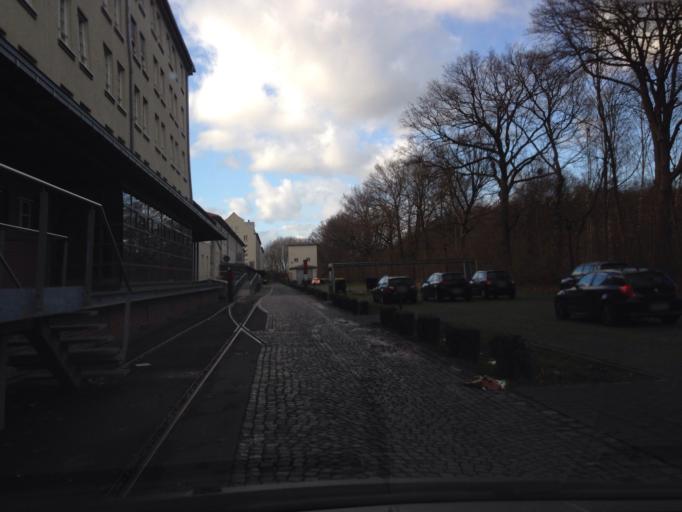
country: DE
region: North Rhine-Westphalia
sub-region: Regierungsbezirk Munster
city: Muenster
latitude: 51.9976
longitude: 7.6352
